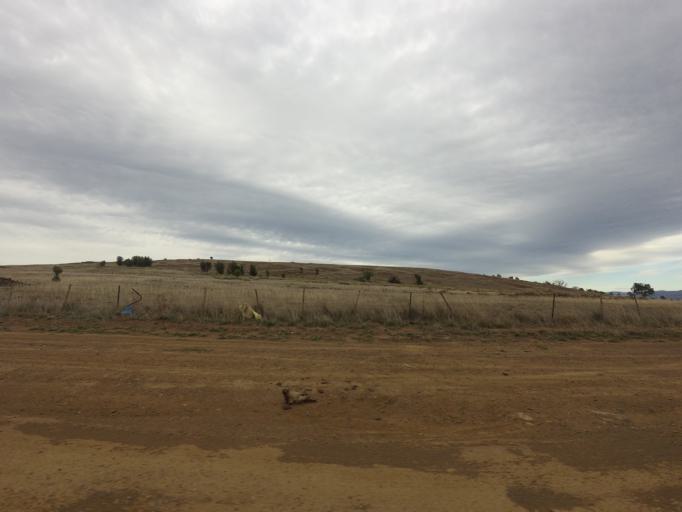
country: AU
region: Tasmania
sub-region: Derwent Valley
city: New Norfolk
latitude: -42.5522
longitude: 146.8989
